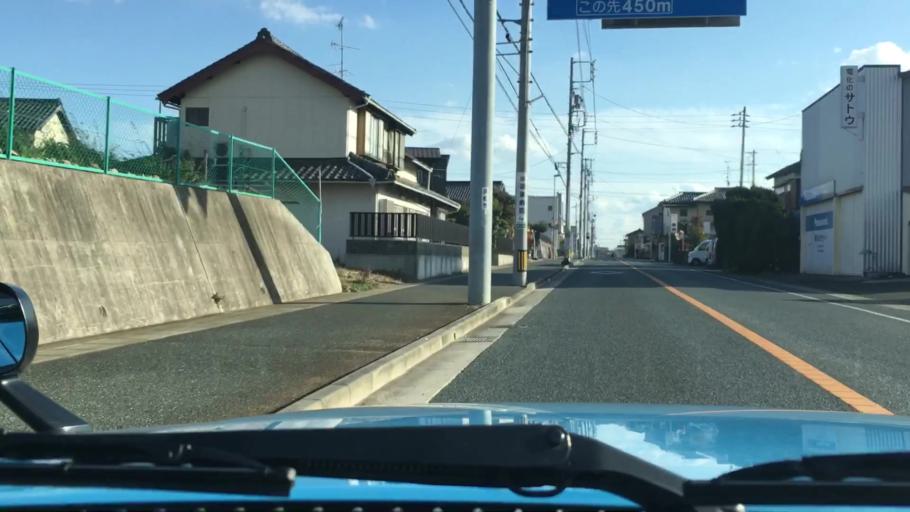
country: JP
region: Shizuoka
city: Hamamatsu
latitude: 34.7561
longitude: 137.6696
